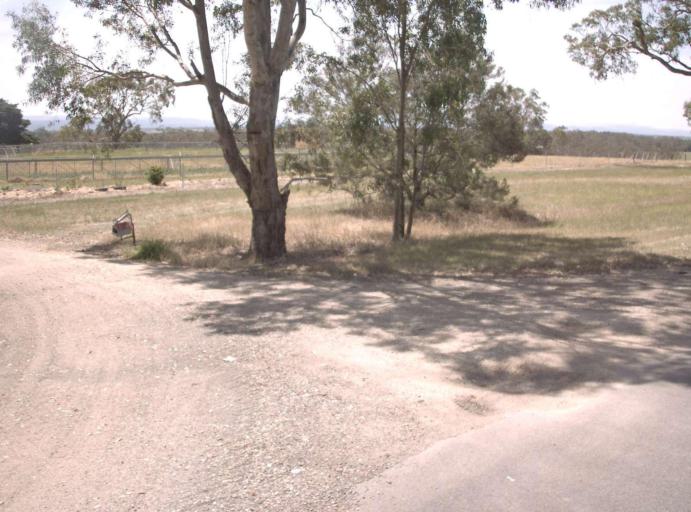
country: AU
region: Victoria
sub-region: Latrobe
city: Traralgon
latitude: -38.1664
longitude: 146.6993
